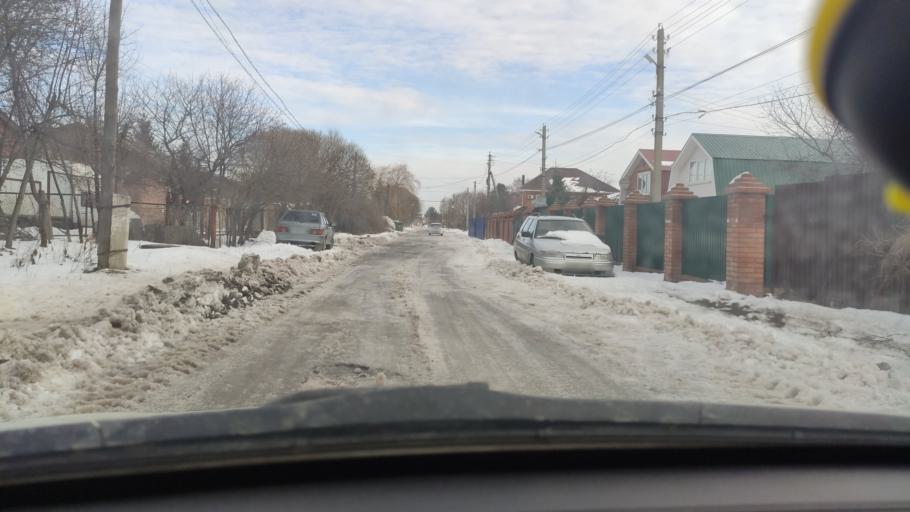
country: RU
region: Samara
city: Tol'yatti
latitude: 53.5626
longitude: 49.3892
